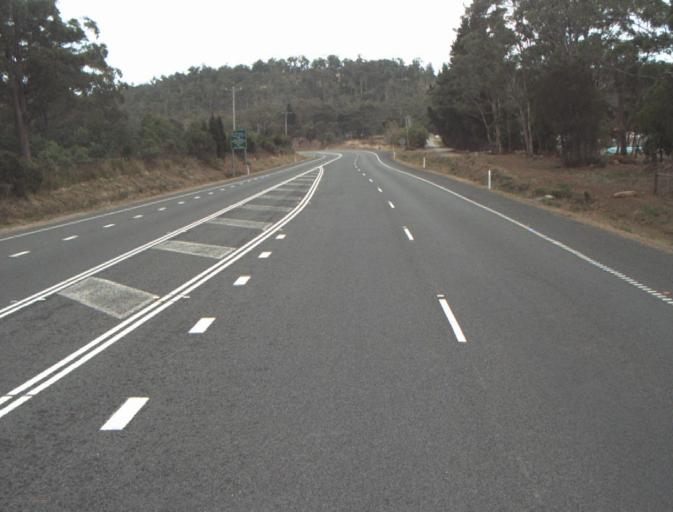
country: AU
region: Tasmania
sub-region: Launceston
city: Mayfield
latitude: -41.2469
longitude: 147.0196
